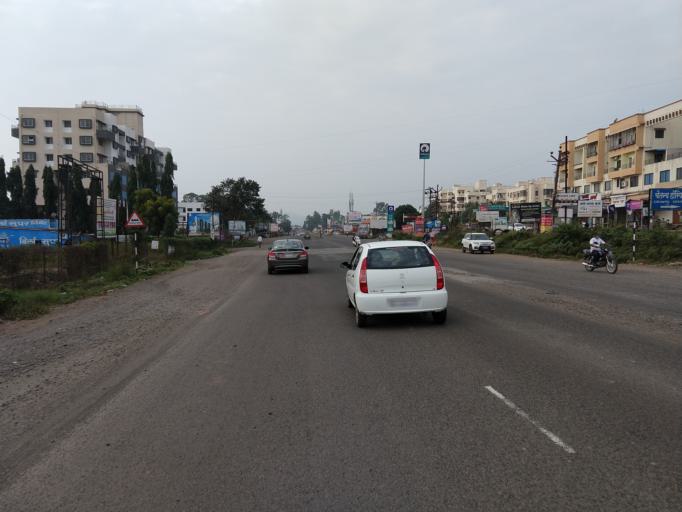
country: IN
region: Maharashtra
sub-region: Pune Division
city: Sasvad
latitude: 18.3544
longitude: 74.0287
